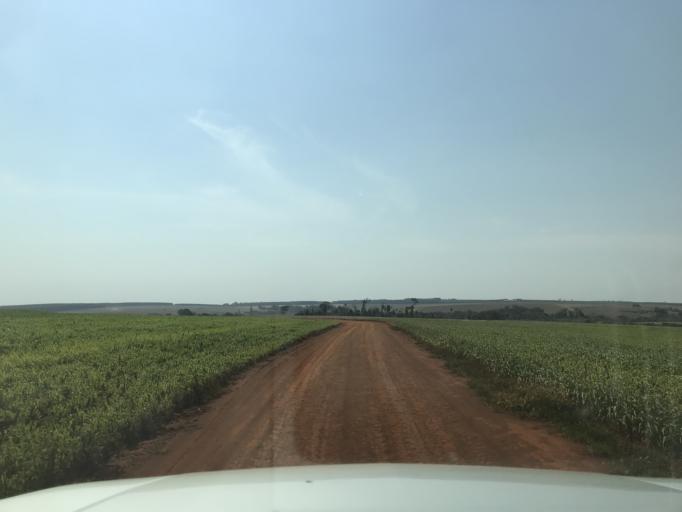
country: BR
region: Parana
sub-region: Palotina
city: Palotina
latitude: -24.2296
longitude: -53.7396
